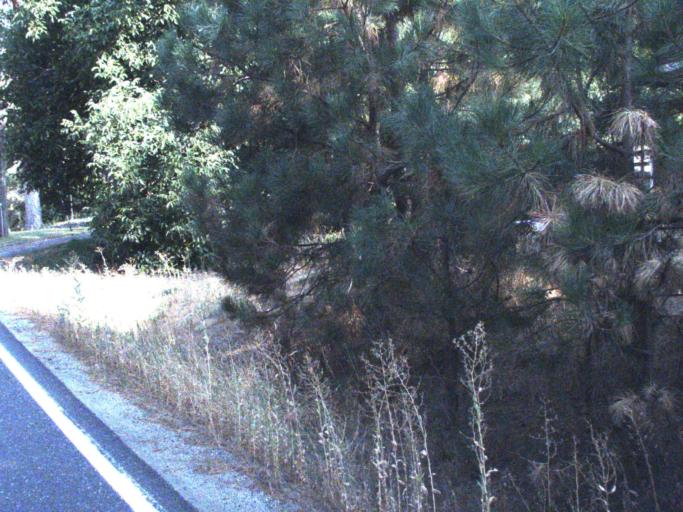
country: US
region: Washington
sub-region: Spokane County
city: Fairwood
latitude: 47.7962
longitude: -117.5341
